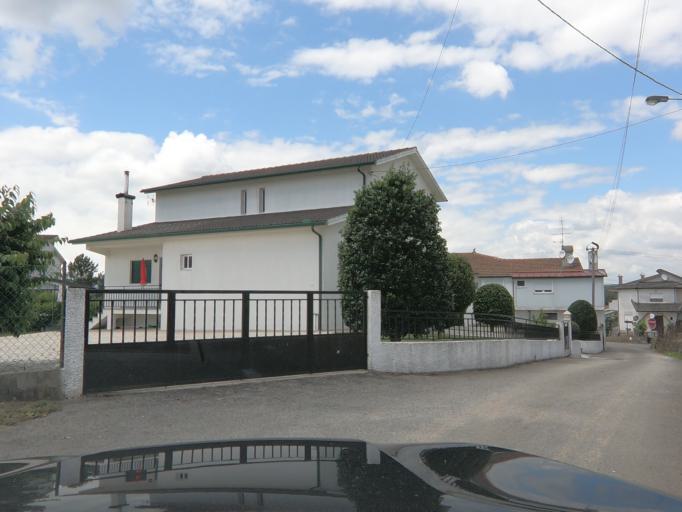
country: PT
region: Vila Real
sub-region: Sabrosa
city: Vilela
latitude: 41.2531
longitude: -7.6682
